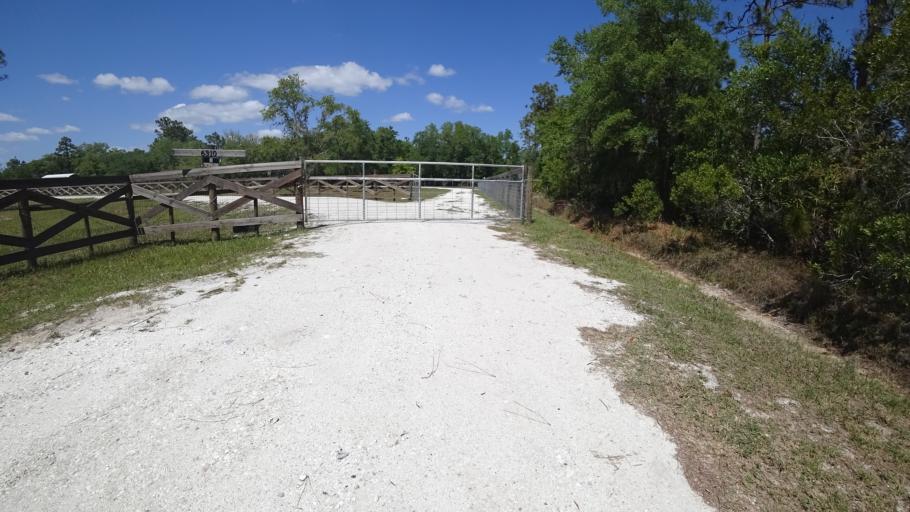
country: US
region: Florida
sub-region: Sarasota County
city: The Meadows
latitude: 27.4267
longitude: -82.3161
